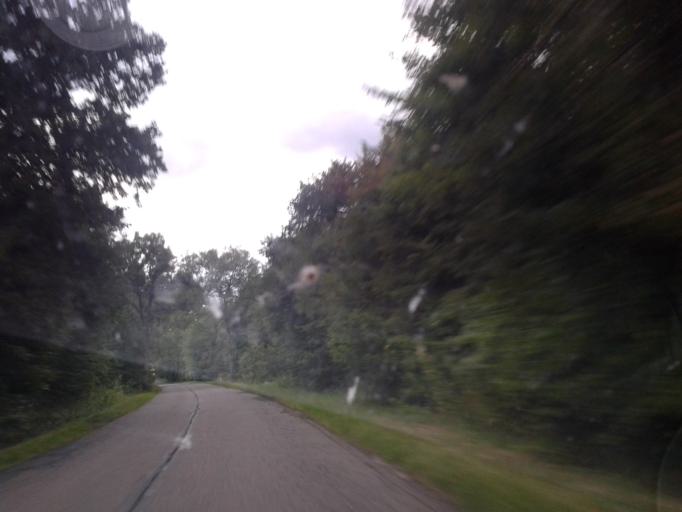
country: PL
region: West Pomeranian Voivodeship
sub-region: Powiat koszalinski
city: Bobolice
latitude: 53.9025
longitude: 16.5360
